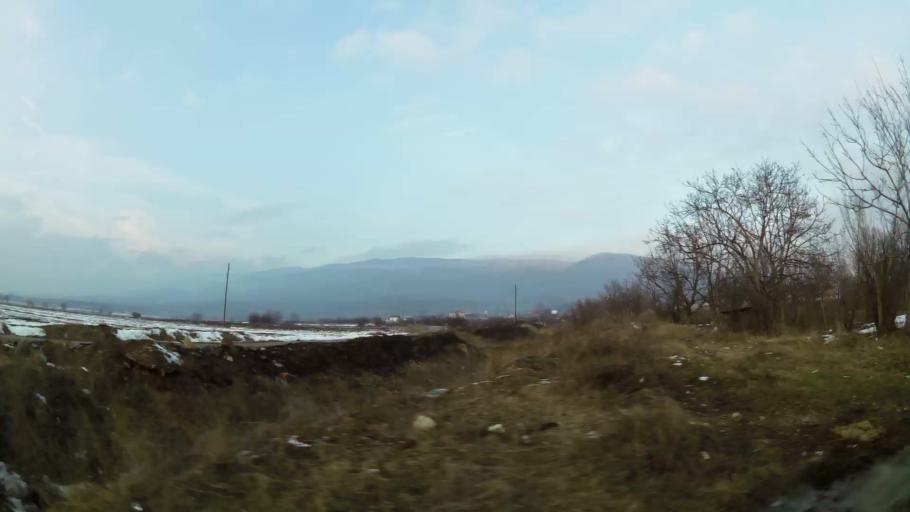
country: MK
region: Aracinovo
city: Arachinovo
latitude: 42.0258
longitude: 21.5449
